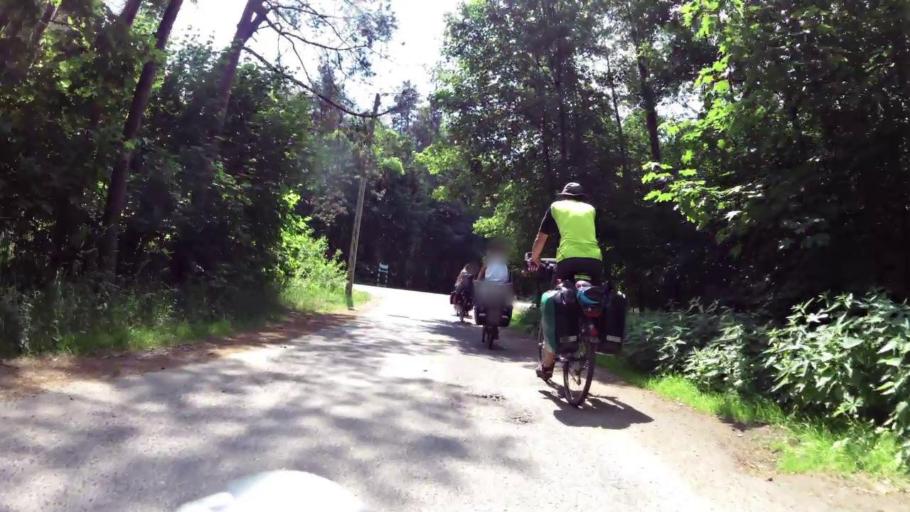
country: PL
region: Kujawsko-Pomorskie
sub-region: Bydgoszcz
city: Fordon
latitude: 53.1387
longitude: 18.1960
